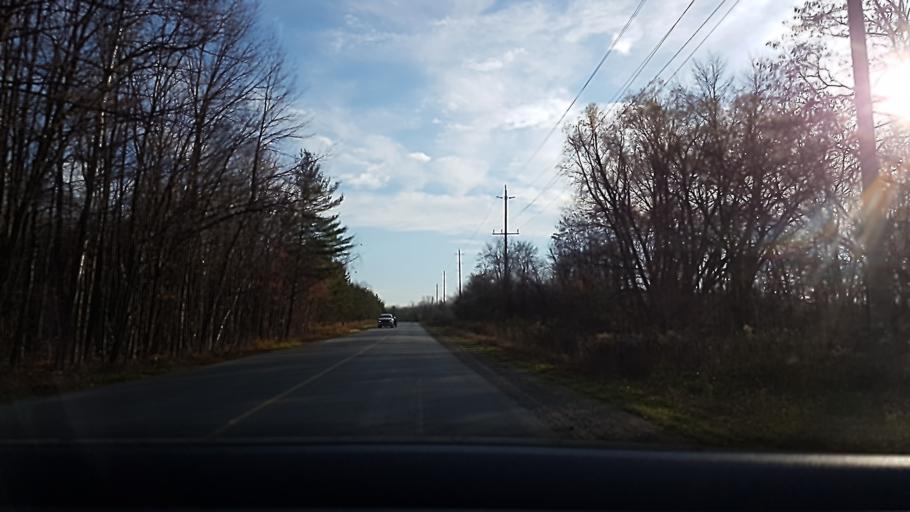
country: CA
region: Ontario
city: Barrie
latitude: 44.3703
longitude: -79.5522
